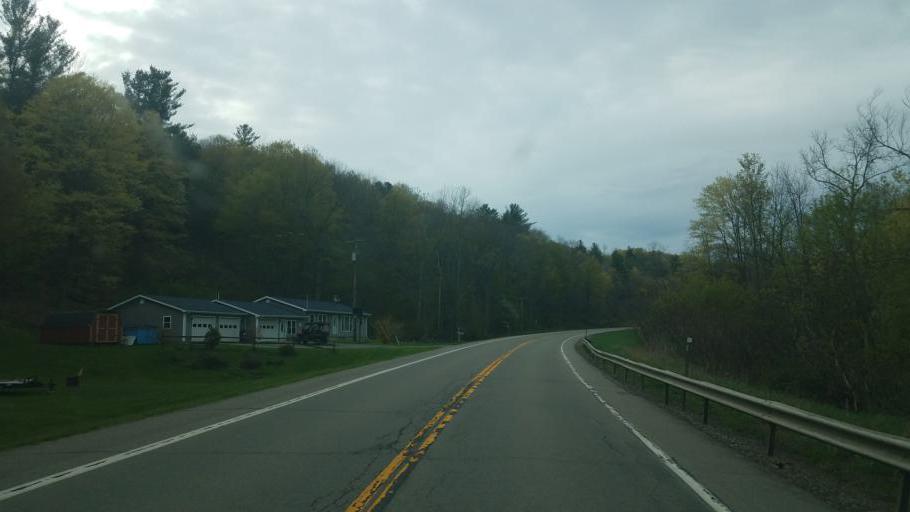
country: US
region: New York
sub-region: Steuben County
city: Canisteo
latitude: 42.1884
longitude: -77.5407
